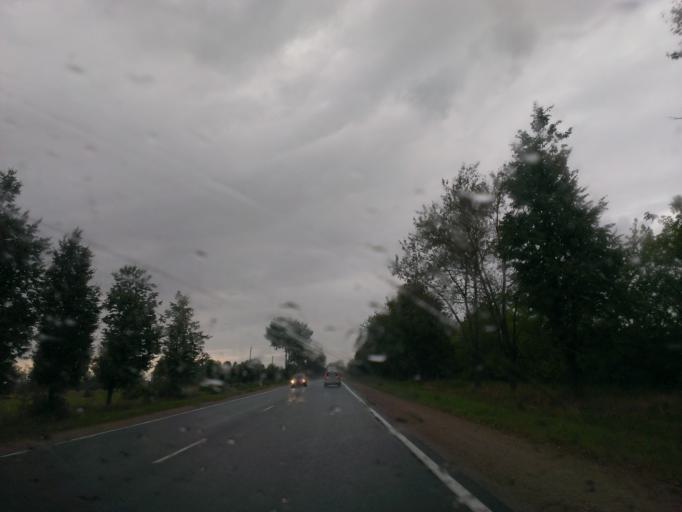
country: LV
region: Ogre
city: Ogre
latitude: 56.7849
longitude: 24.6456
